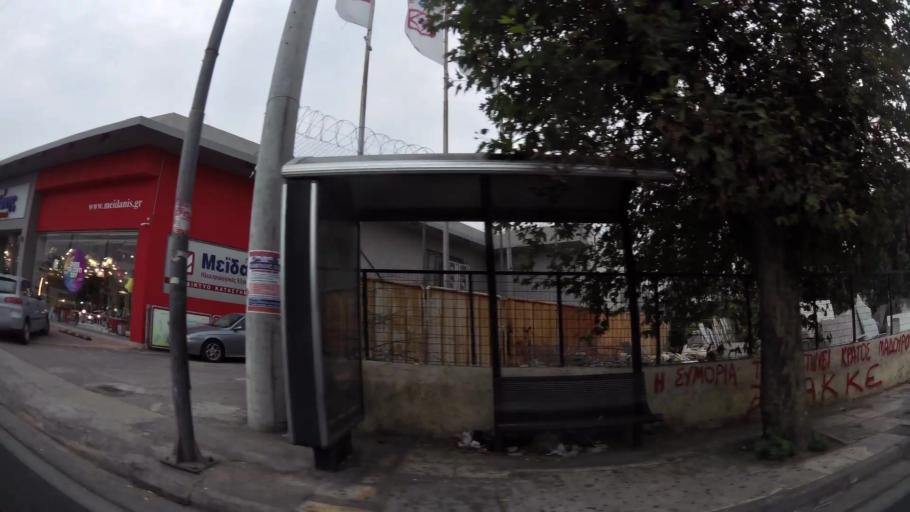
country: GR
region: Attica
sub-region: Nomarchia Athinas
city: Aigaleo
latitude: 37.9764
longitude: 23.6752
